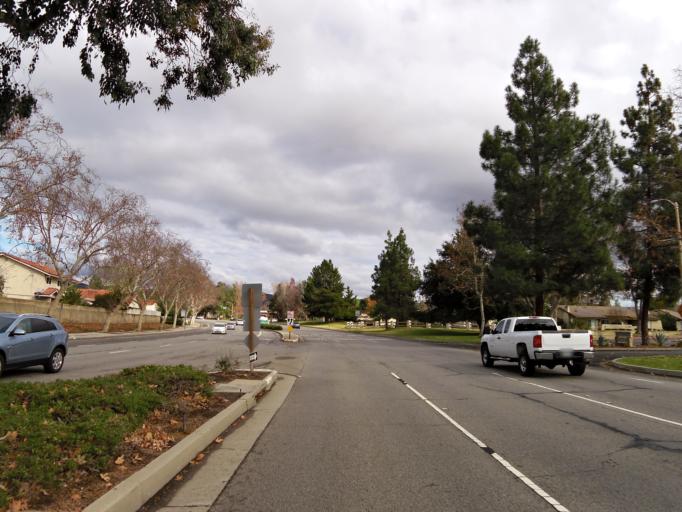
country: US
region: California
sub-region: Ventura County
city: Thousand Oaks
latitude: 34.1505
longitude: -118.8309
